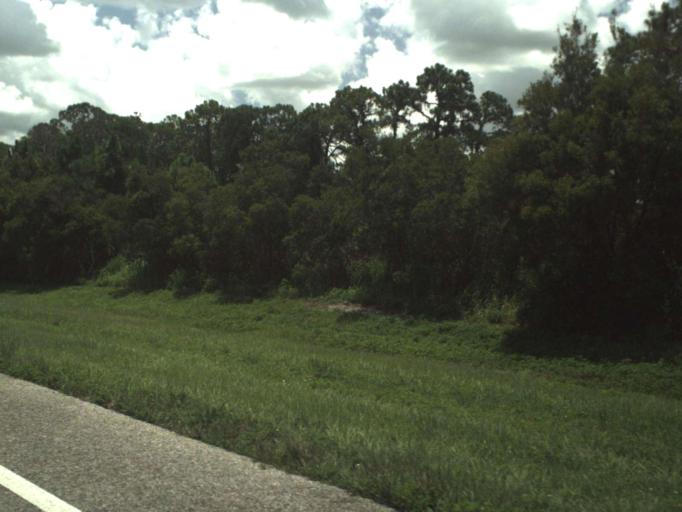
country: US
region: Florida
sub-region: Indian River County
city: Fellsmere
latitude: 27.6805
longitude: -80.8274
